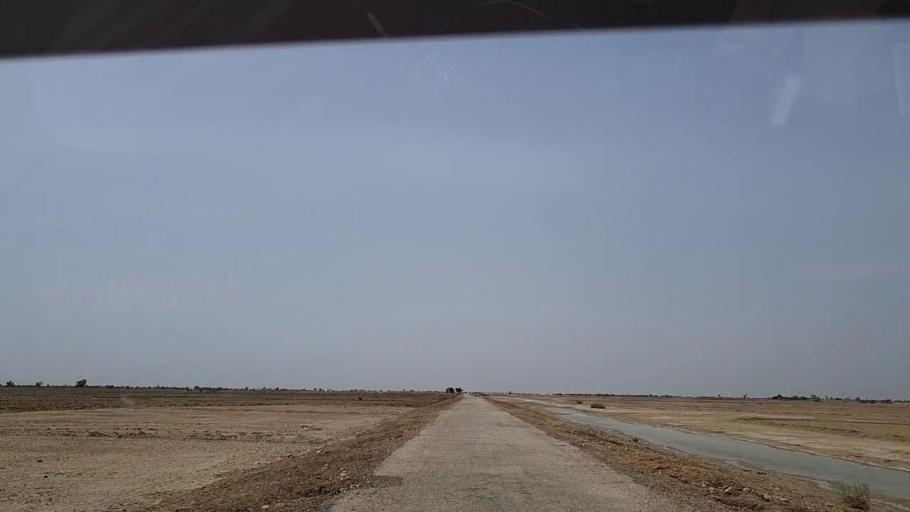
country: PK
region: Sindh
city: Johi
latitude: 26.7263
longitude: 67.6413
